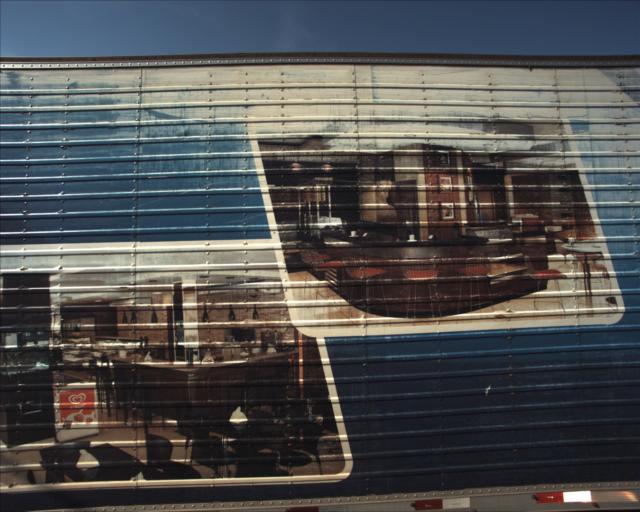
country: BR
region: Sao Paulo
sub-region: Sorocaba
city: Sorocaba
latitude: -23.4873
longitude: -47.4444
